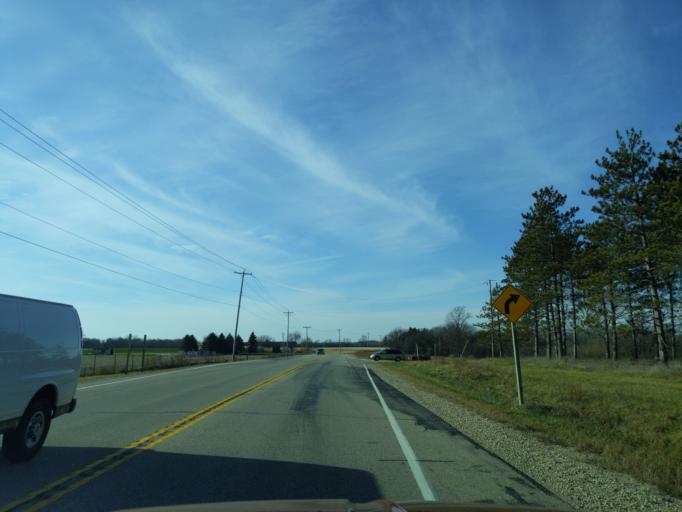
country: US
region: Wisconsin
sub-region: Jefferson County
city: Palmyra
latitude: 42.7958
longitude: -88.6229
